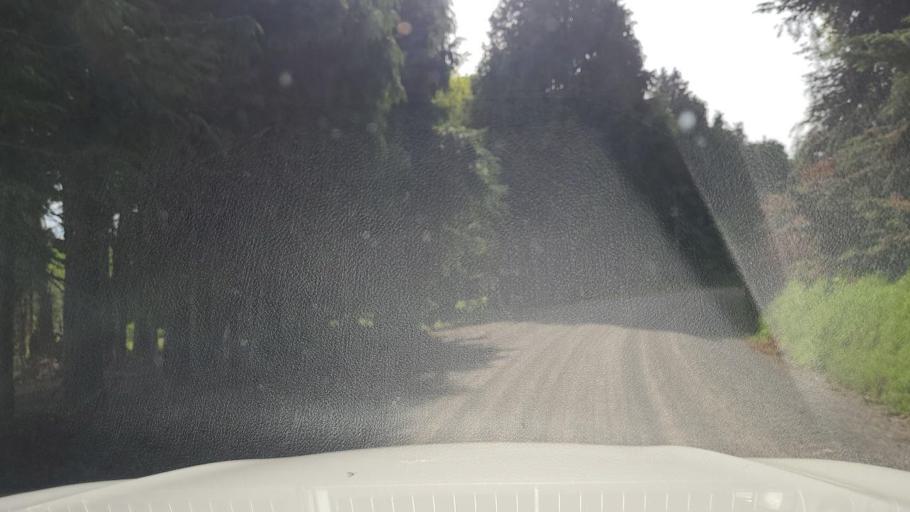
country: NZ
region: Hawke's Bay
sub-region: Napier City
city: Taradale
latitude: -39.3387
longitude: 176.6562
